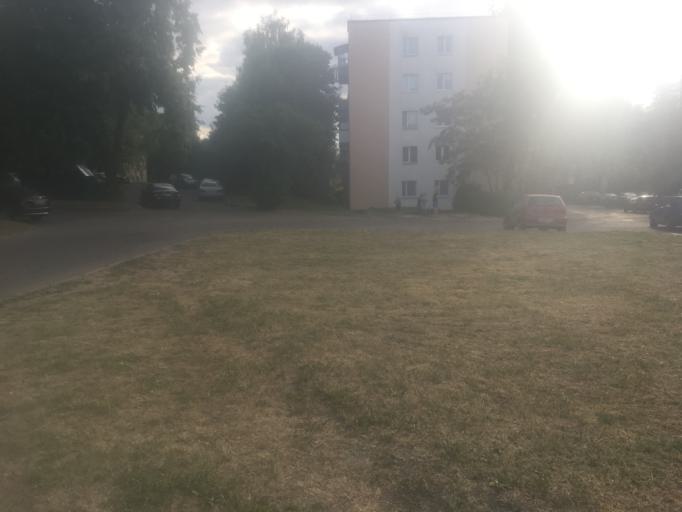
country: BY
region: Grodnenskaya
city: Hrodna
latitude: 53.7012
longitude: 23.8060
